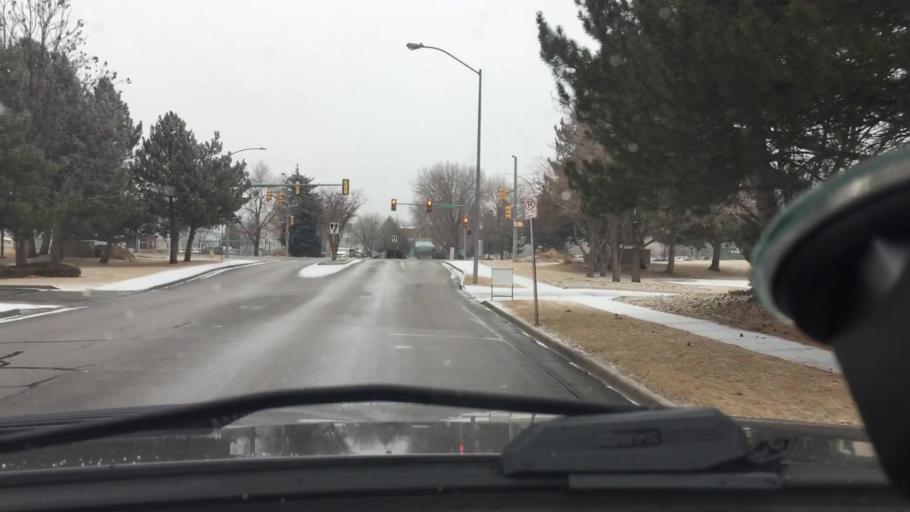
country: US
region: Colorado
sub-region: Larimer County
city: Fort Collins
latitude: 40.5666
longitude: -105.0336
